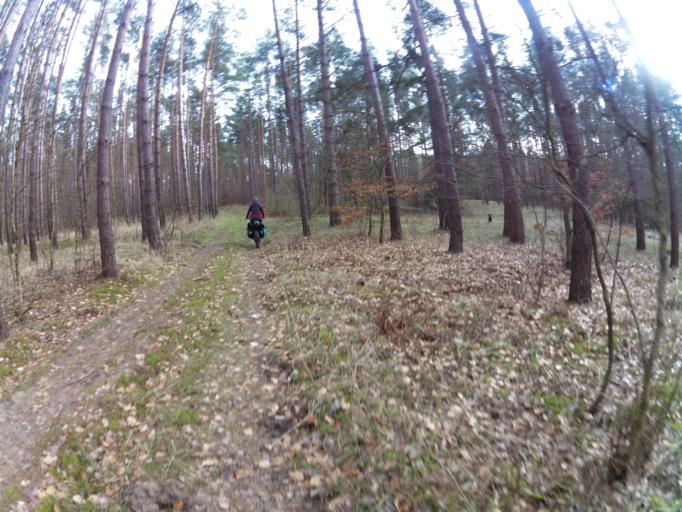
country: PL
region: Lubusz
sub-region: Powiat gorzowski
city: Lubiszyn
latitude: 52.7744
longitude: 14.8424
